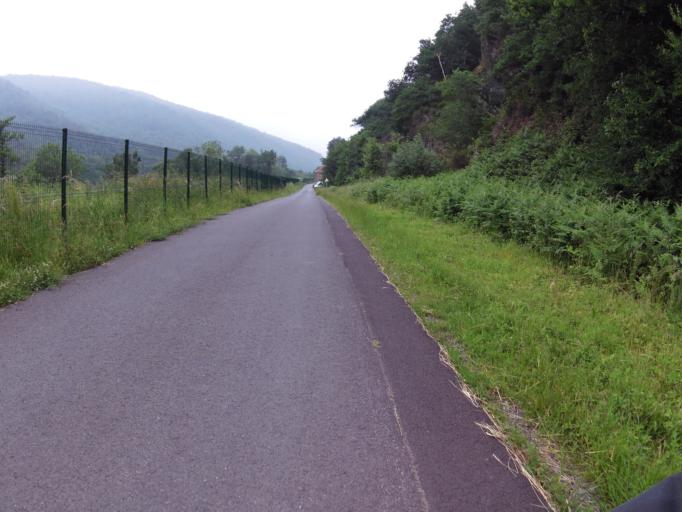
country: FR
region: Champagne-Ardenne
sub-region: Departement des Ardennes
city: Revin
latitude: 49.9512
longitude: 4.6547
